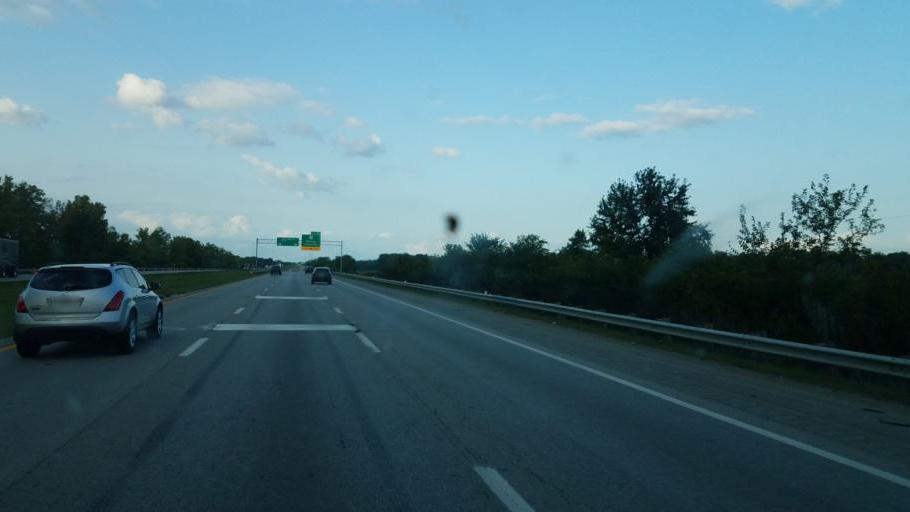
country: US
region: Ohio
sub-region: Franklin County
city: Groveport
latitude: 39.8903
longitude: -82.9097
